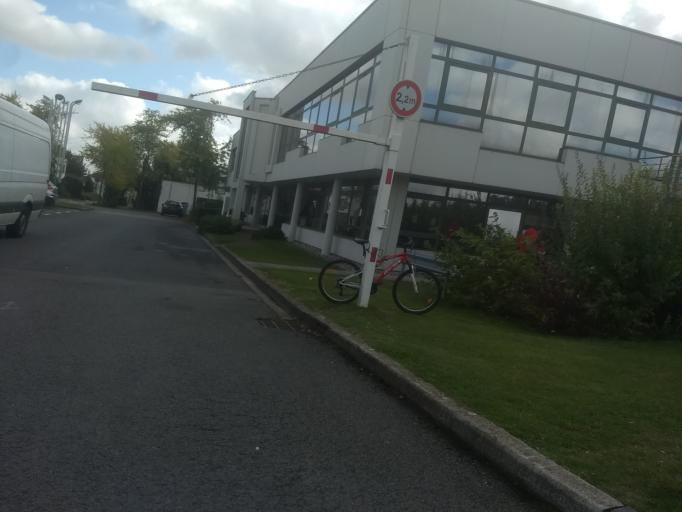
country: FR
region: Nord-Pas-de-Calais
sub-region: Departement du Pas-de-Calais
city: Anzin-Saint-Aubin
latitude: 50.3029
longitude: 2.7314
